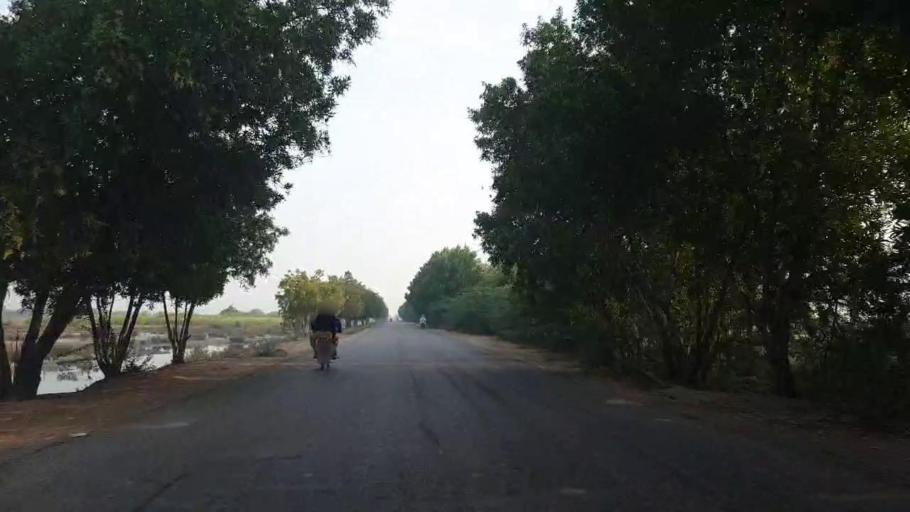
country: PK
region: Sindh
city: Badin
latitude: 24.6823
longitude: 68.9109
